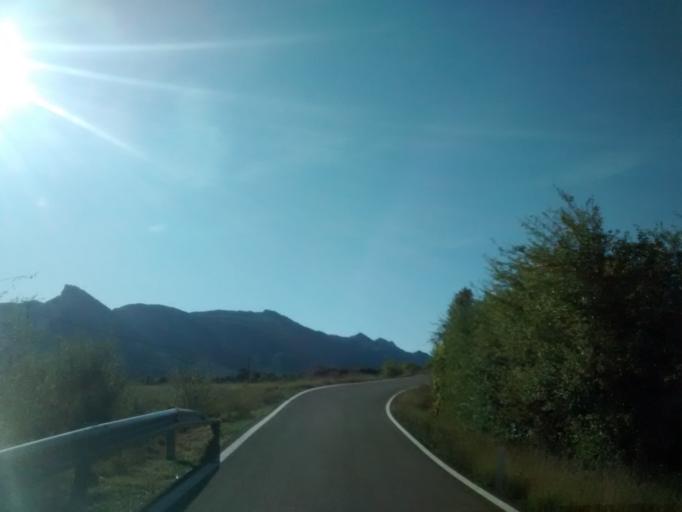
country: ES
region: Aragon
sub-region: Provincia de Zaragoza
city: Santa Eulalia de Gallego
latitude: 42.3903
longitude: -0.7232
